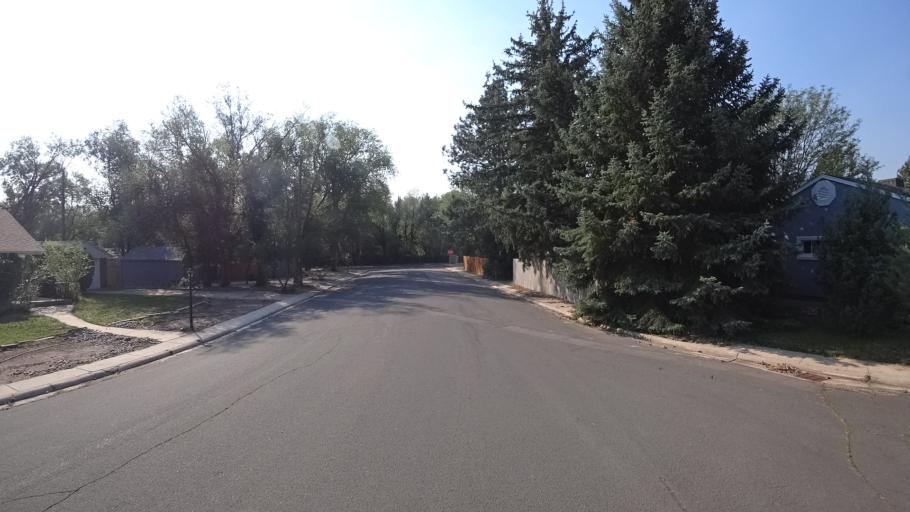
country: US
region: Colorado
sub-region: El Paso County
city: Colorado Springs
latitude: 38.8033
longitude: -104.8384
